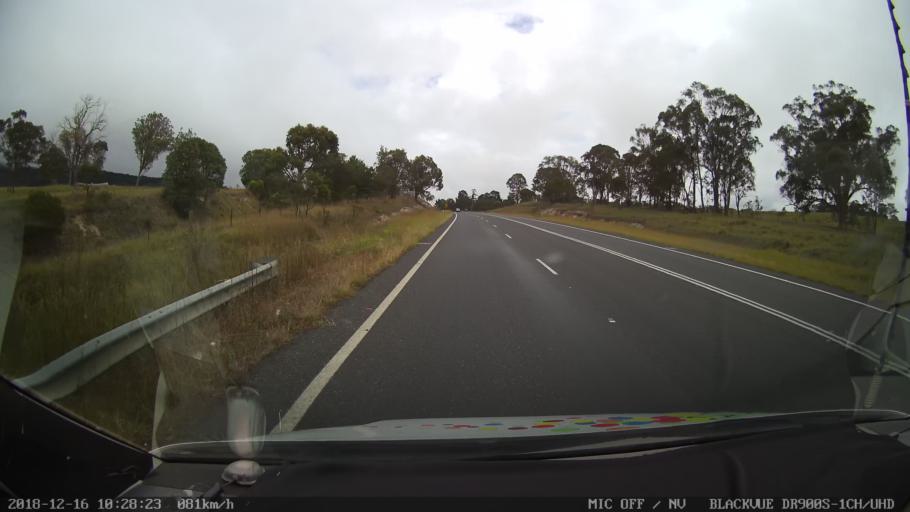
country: AU
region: New South Wales
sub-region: Tenterfield Municipality
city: Carrolls Creek
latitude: -29.1219
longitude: 151.9973
